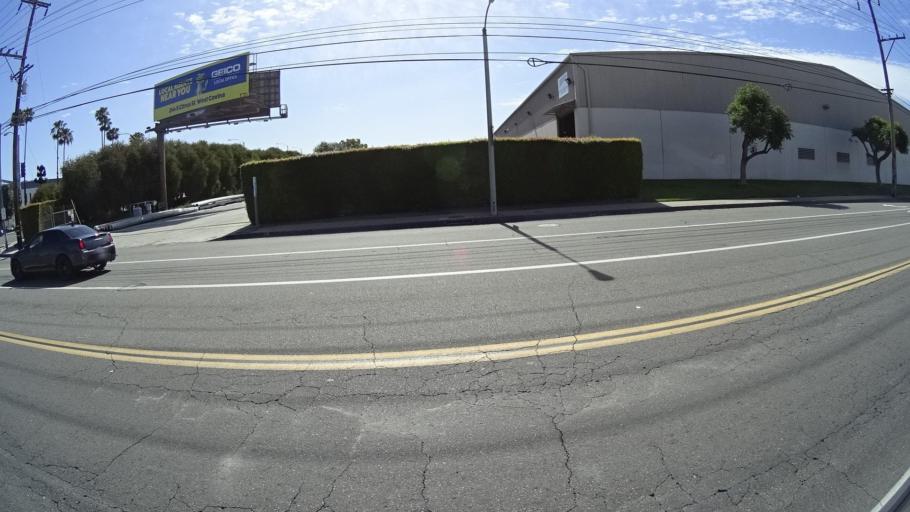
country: US
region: California
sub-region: Los Angeles County
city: La Puente
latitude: 34.0152
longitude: -117.9531
